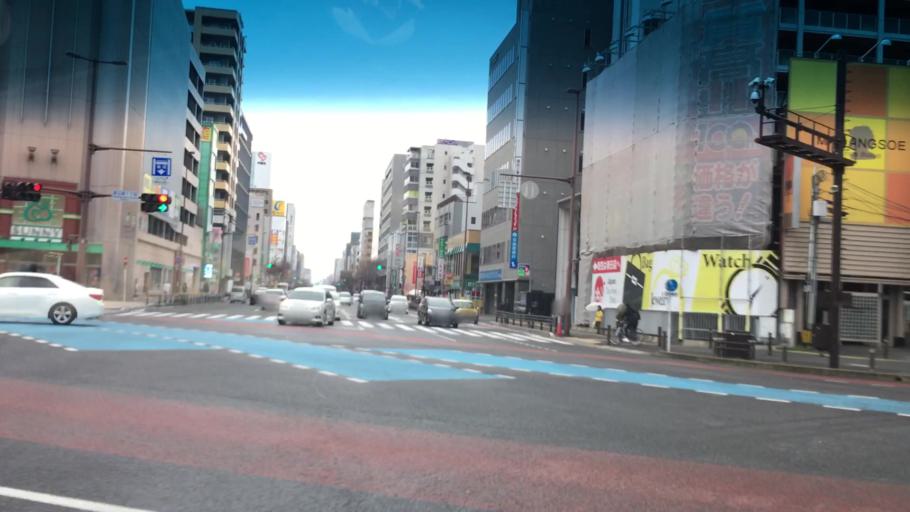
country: JP
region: Fukuoka
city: Fukuoka-shi
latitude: 33.5826
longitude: 130.4059
